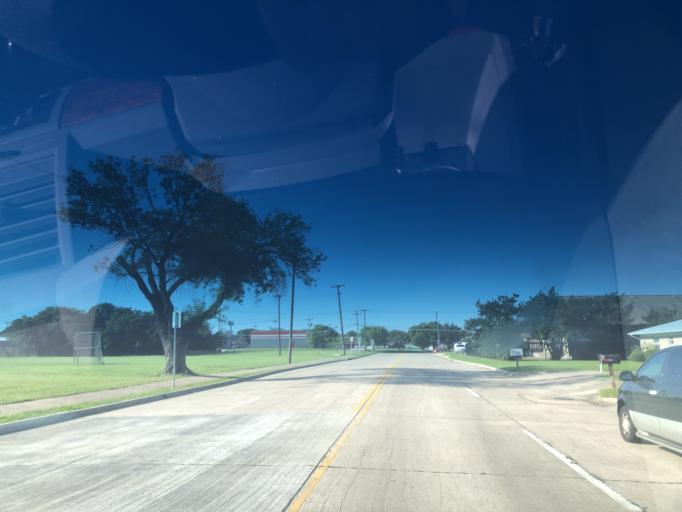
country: US
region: Texas
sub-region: Dallas County
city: Grand Prairie
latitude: 32.7118
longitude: -97.0018
